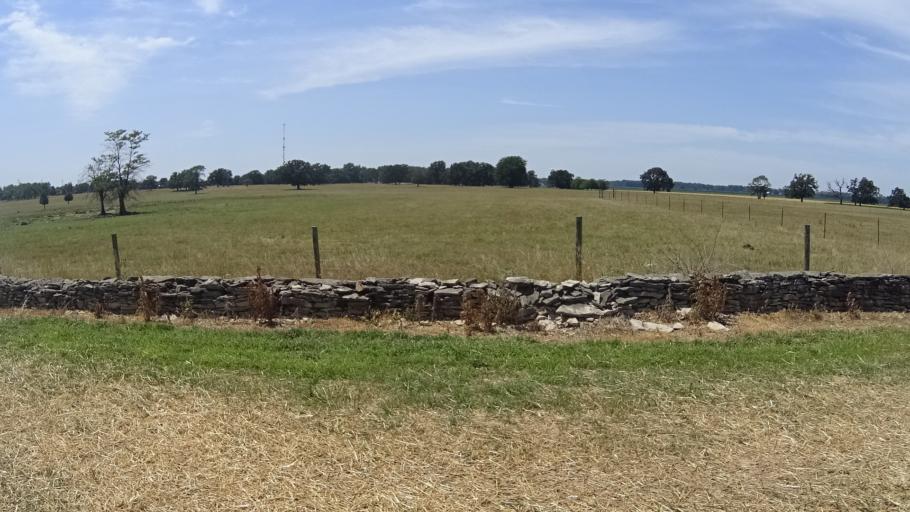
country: US
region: Ohio
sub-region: Erie County
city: Sandusky
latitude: 41.4098
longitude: -82.7715
